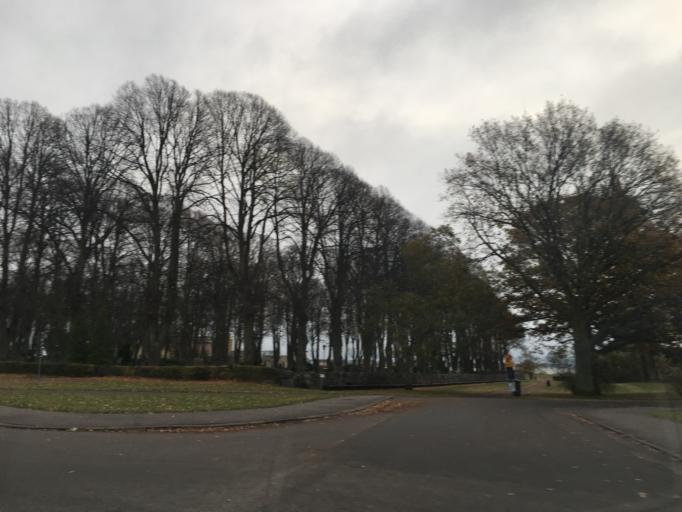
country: SE
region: Kalmar
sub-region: Kalmar Kommun
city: Kalmar
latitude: 56.6577
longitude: 16.3477
